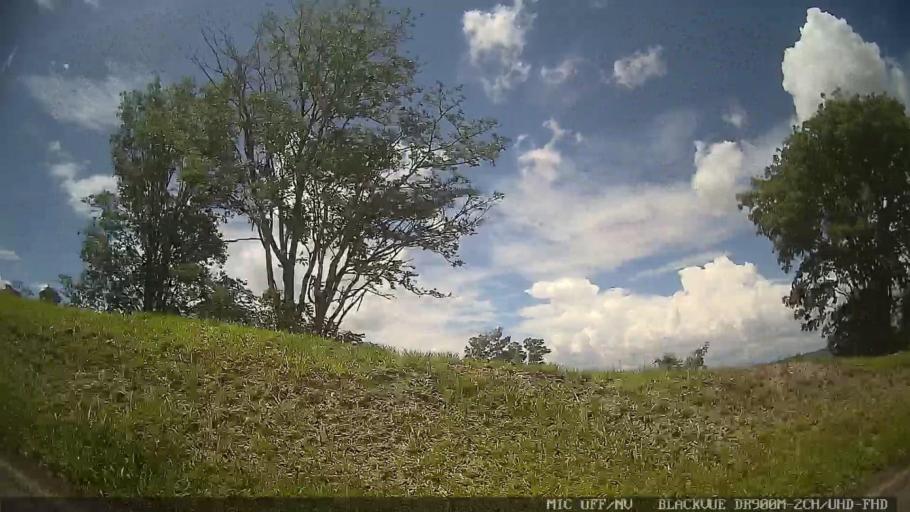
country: BR
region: Sao Paulo
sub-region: Conchas
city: Conchas
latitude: -23.0260
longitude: -47.9994
